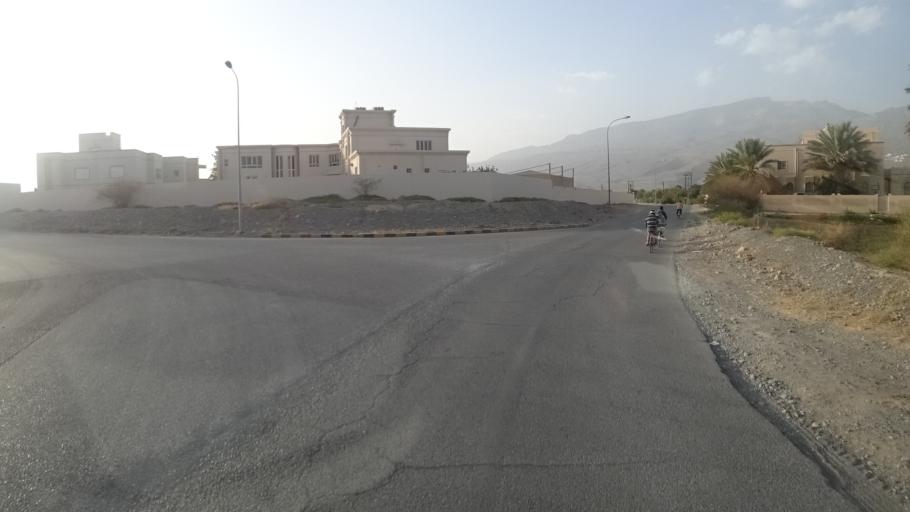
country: OM
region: Muhafazat ad Dakhiliyah
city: Bahla'
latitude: 23.1011
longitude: 57.3025
